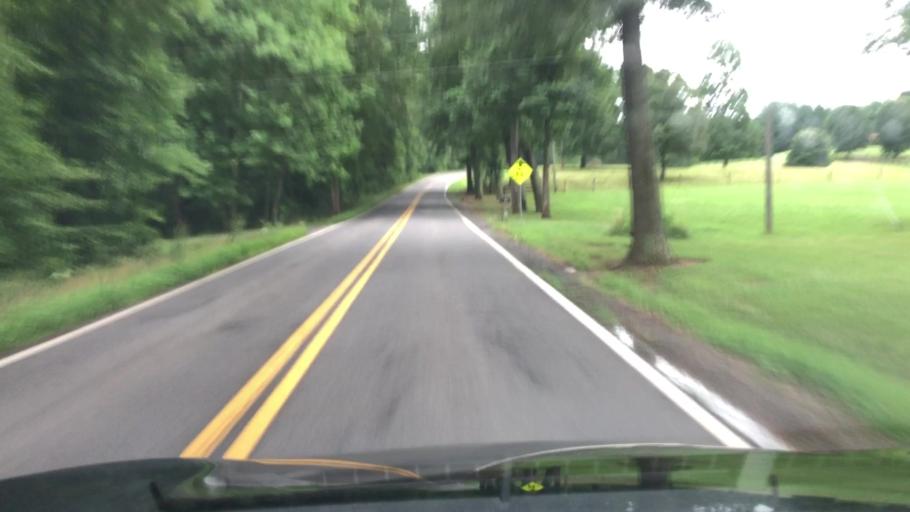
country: US
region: Virginia
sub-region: Fauquier County
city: Bealeton
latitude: 38.5360
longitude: -77.6115
